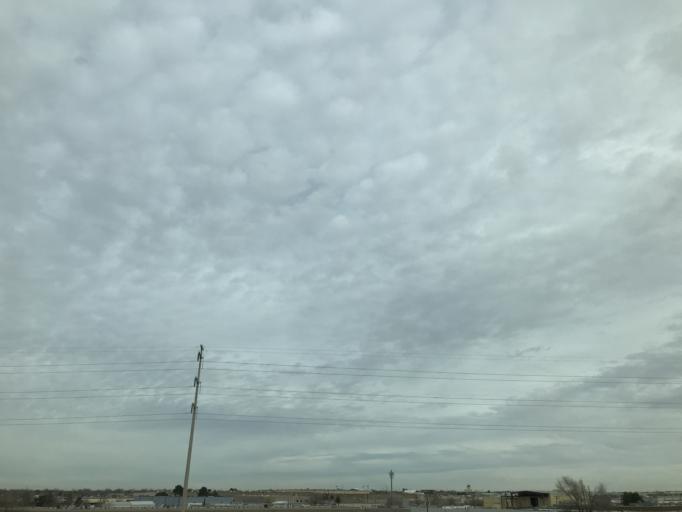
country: US
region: Colorado
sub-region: Adams County
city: Commerce City
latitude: 39.7837
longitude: -104.9177
